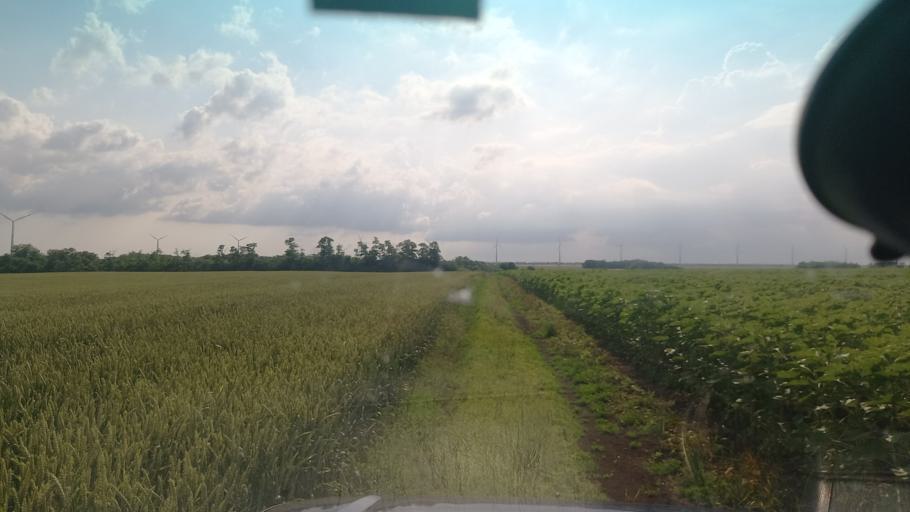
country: RU
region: Adygeya
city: Giaginskaya
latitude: 44.9571
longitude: 40.1125
